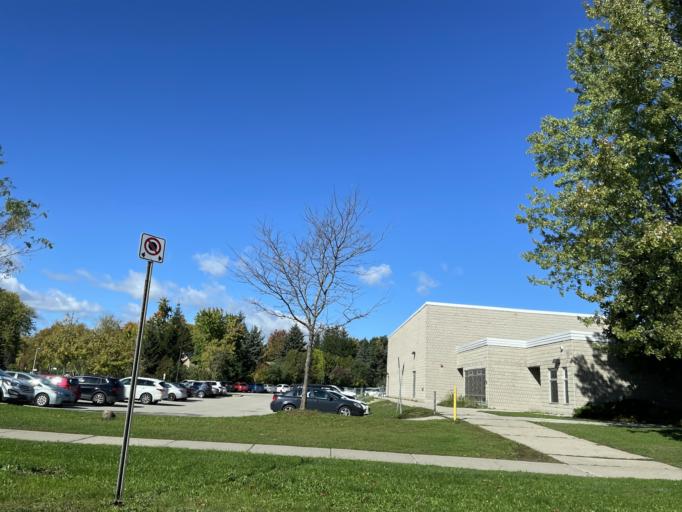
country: CA
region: Ontario
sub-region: Wellington County
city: Guelph
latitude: 43.5337
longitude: -80.2878
